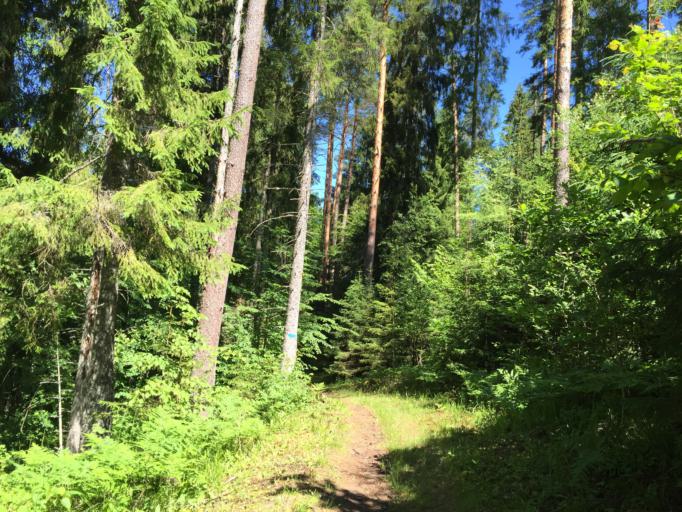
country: LV
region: Sigulda
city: Sigulda
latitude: 57.2218
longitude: 24.9082
